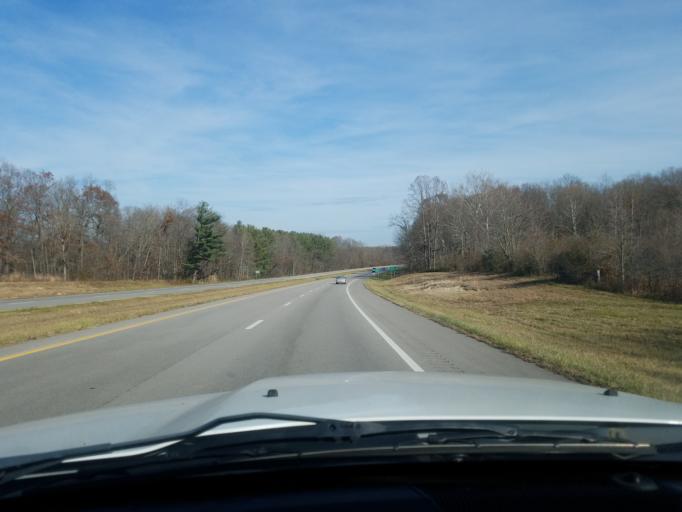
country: US
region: Ohio
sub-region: Athens County
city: Athens
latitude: 39.2021
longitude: -82.2615
